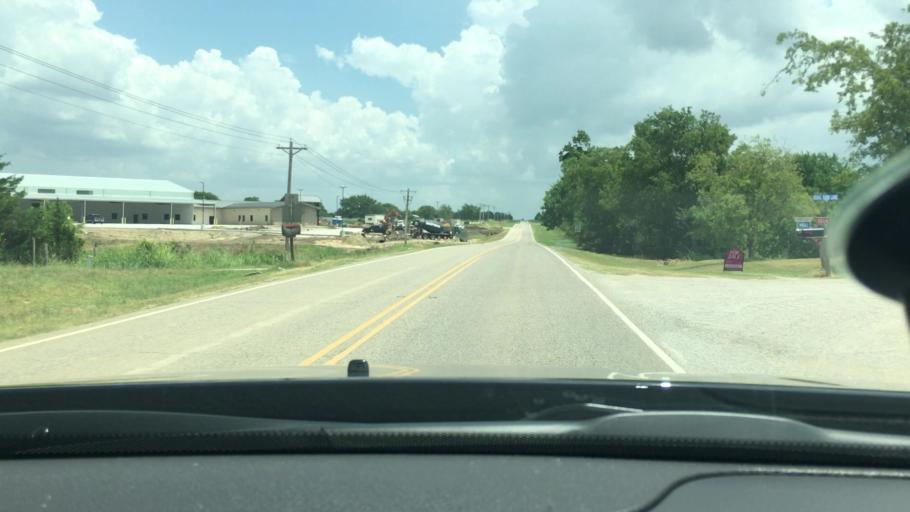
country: US
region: Oklahoma
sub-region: Love County
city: Marietta
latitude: 33.9403
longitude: -97.0879
